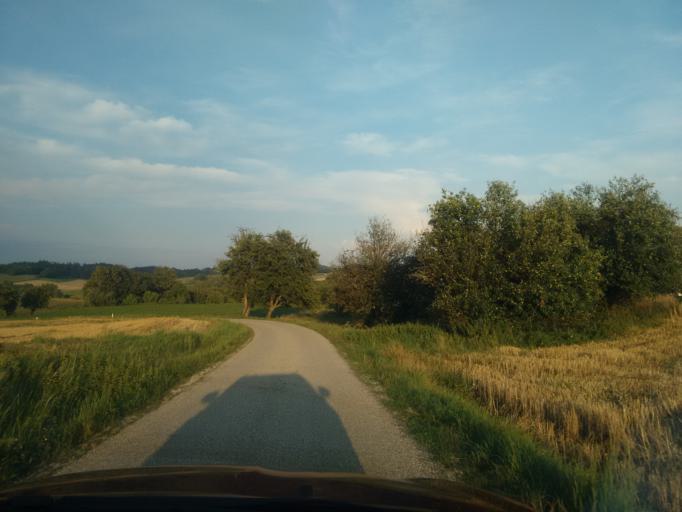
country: AT
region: Upper Austria
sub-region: Politischer Bezirk Grieskirchen
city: Bad Schallerbach
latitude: 48.1987
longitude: 13.9145
